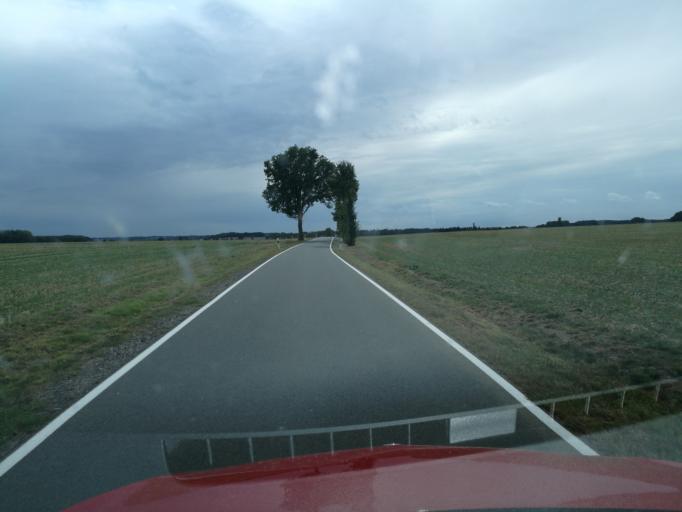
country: DE
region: Saxony
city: Oschatz
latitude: 51.2790
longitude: 13.0817
